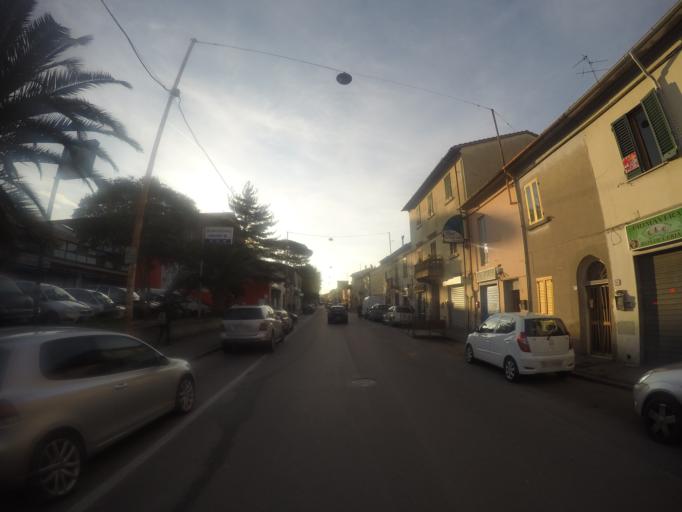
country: IT
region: Tuscany
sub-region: Provincia di Prato
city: Prato
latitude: 43.8857
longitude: 11.0859
